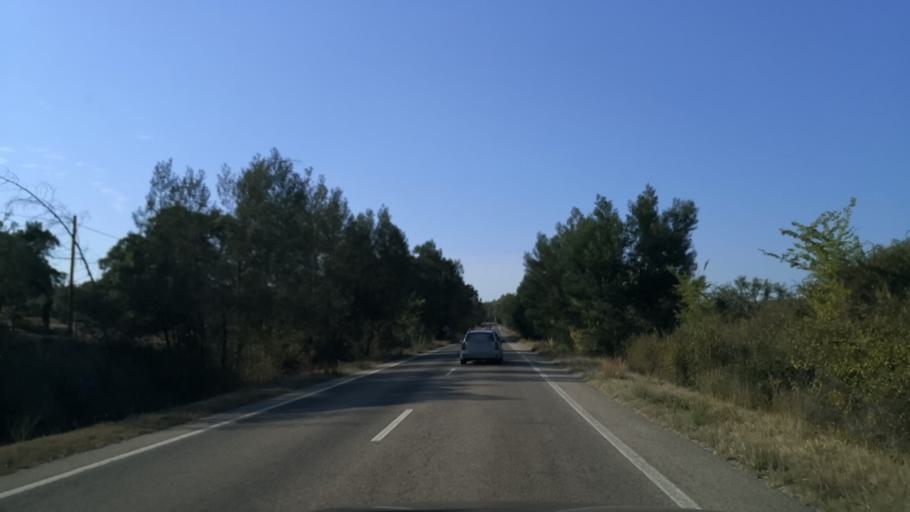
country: PT
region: Santarem
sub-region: Almeirim
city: Fazendas de Almeirim
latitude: 39.0912
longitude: -8.5736
